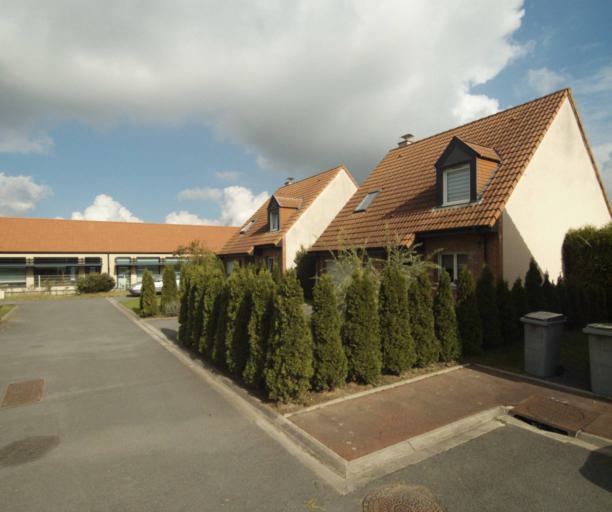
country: FR
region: Nord-Pas-de-Calais
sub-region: Departement du Nord
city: Herlies
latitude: 50.5799
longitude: 2.8566
